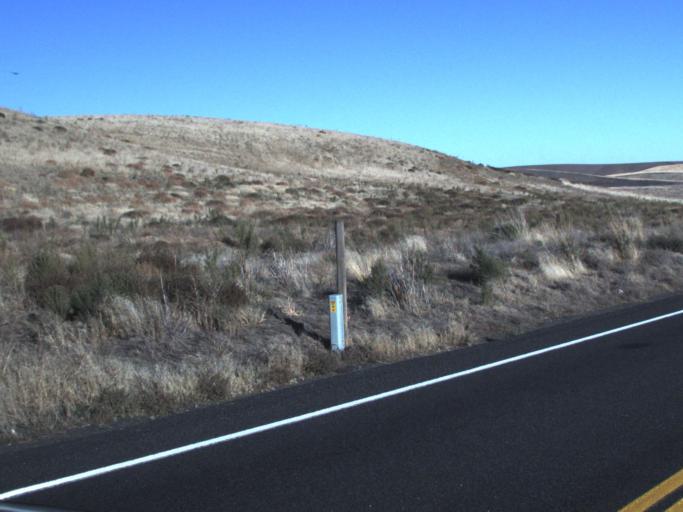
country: US
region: Washington
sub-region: Adams County
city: Ritzville
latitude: 46.8091
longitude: -118.3084
